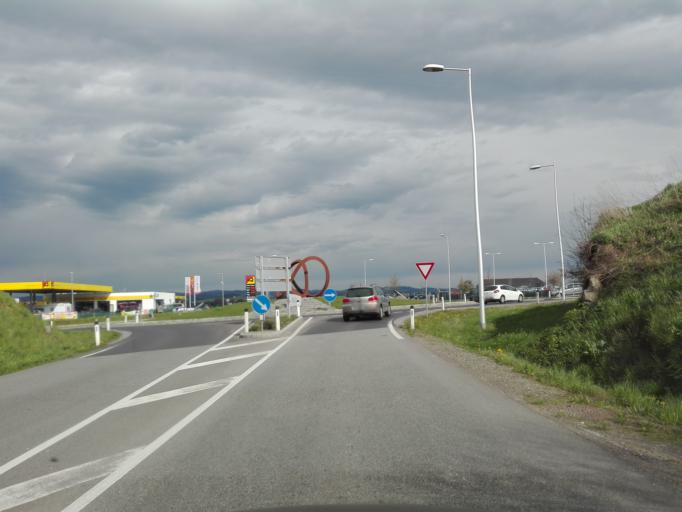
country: AT
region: Upper Austria
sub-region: Politischer Bezirk Rohrbach
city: Atzesberg
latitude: 48.4967
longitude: 13.9694
